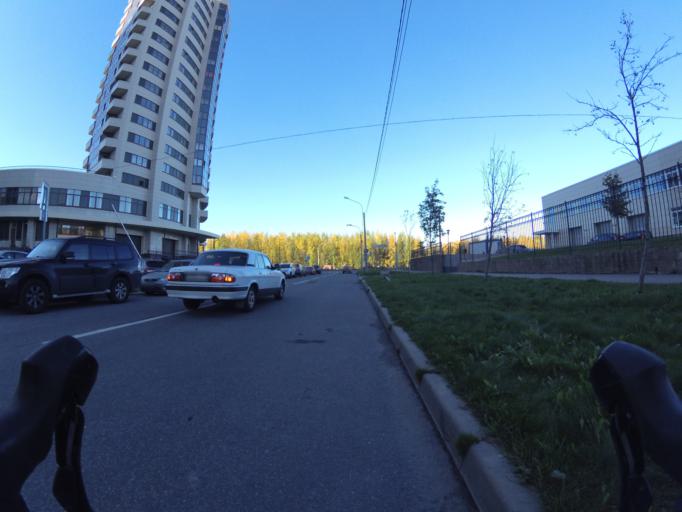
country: RU
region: Leningrad
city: Untolovo
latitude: 60.0003
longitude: 30.1956
